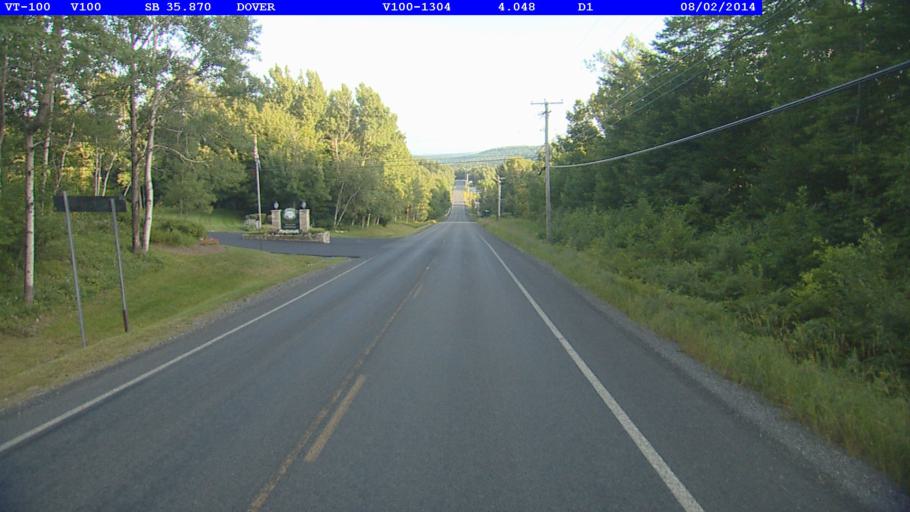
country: US
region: Vermont
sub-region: Windham County
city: Dover
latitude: 42.9695
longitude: -72.8875
